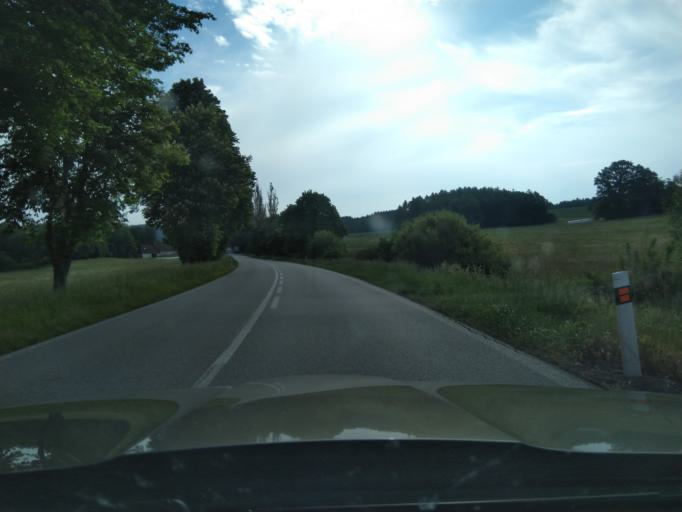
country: CZ
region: Jihocesky
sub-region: Okres Prachatice
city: Strunkovice nad Blanici
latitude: 49.0530
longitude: 14.0994
